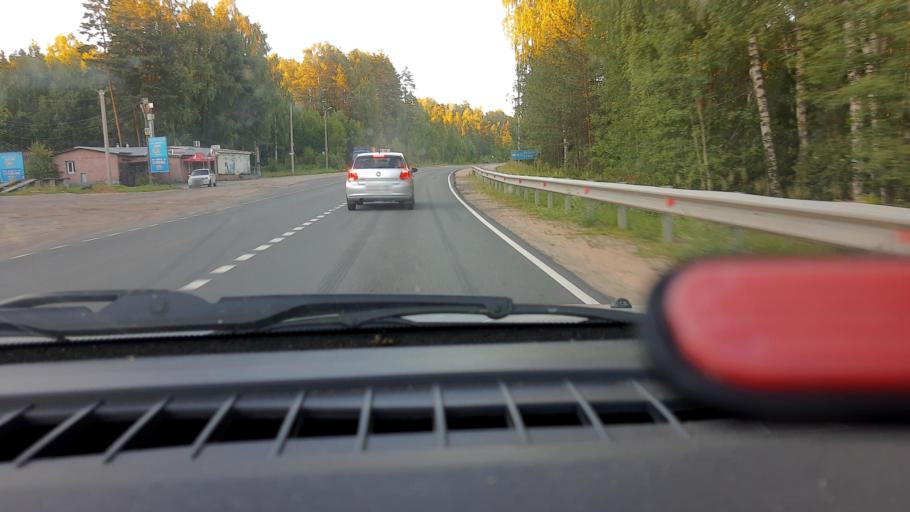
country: RU
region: Nizjnij Novgorod
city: Krasnyye Baki
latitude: 57.1381
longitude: 45.2206
